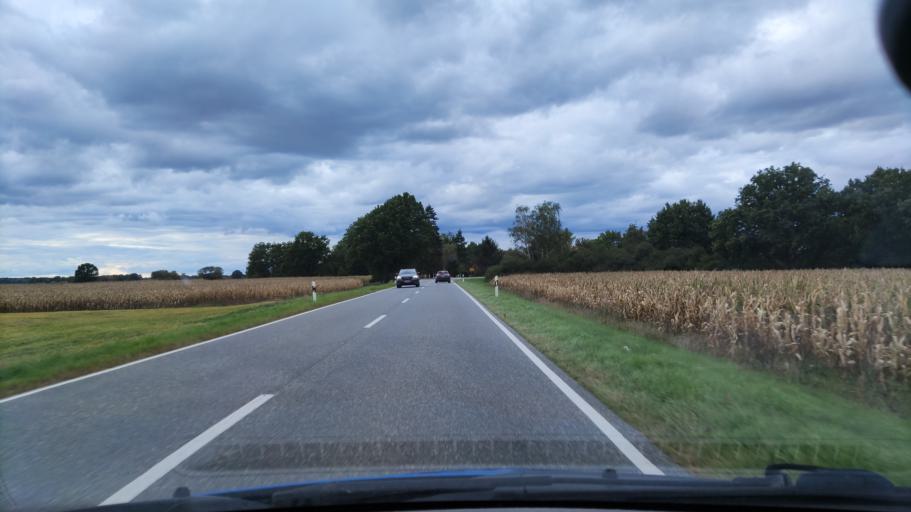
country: DE
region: Lower Saxony
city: Neu Darchau
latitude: 53.3087
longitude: 10.9607
